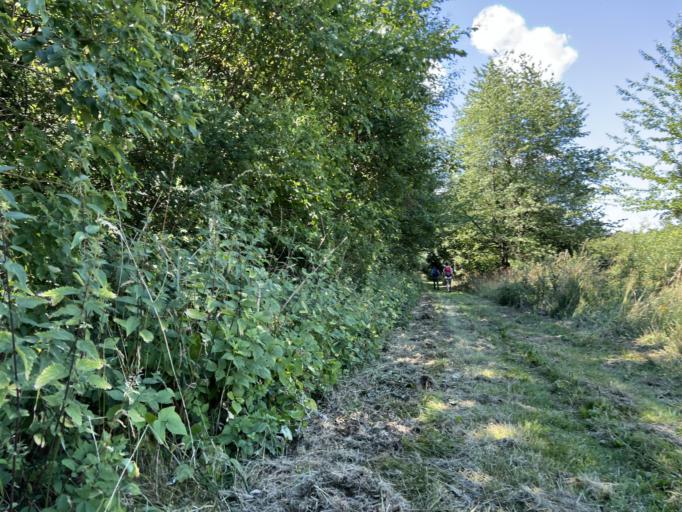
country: DE
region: Hesse
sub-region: Regierungsbezirk Darmstadt
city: Steinau an der Strasse
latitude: 50.3015
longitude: 9.4868
